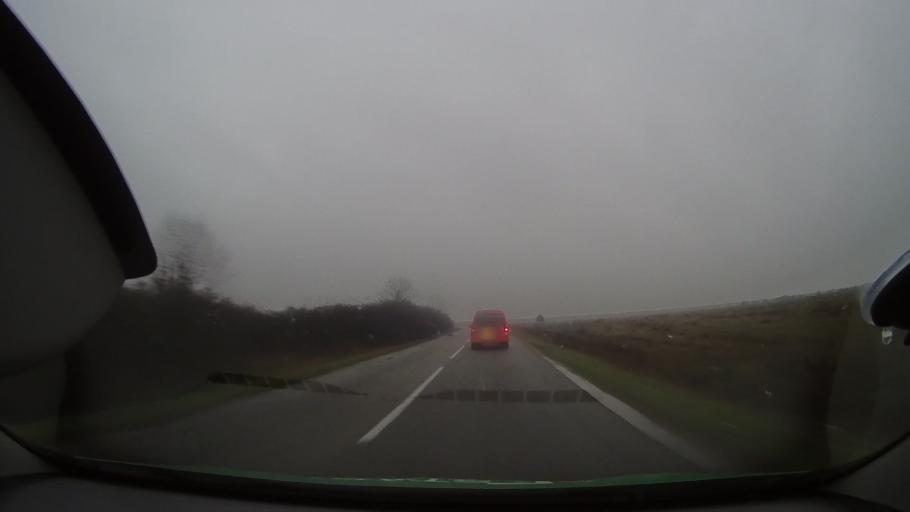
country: RO
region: Arad
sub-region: Comuna Craiova
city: Craiova
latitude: 46.6145
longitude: 21.9568
